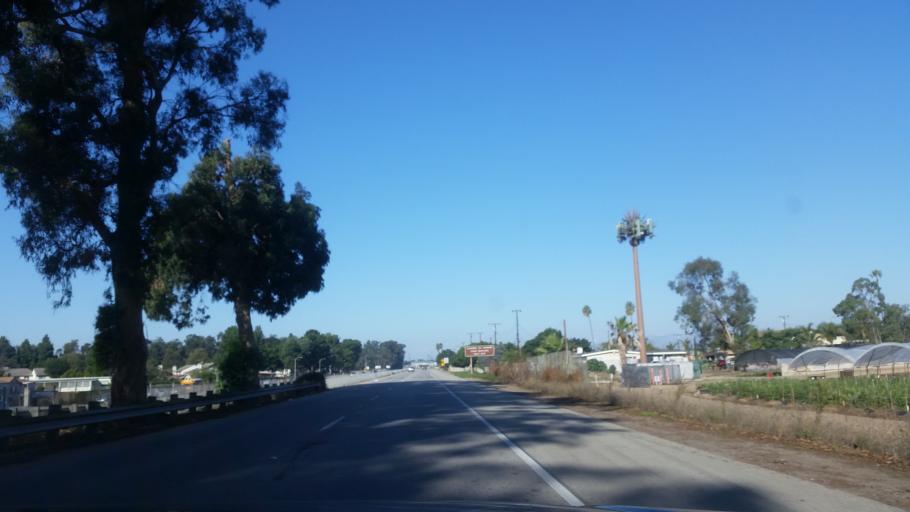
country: US
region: California
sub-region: Ventura County
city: Oxnard
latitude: 34.1670
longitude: -119.1464
